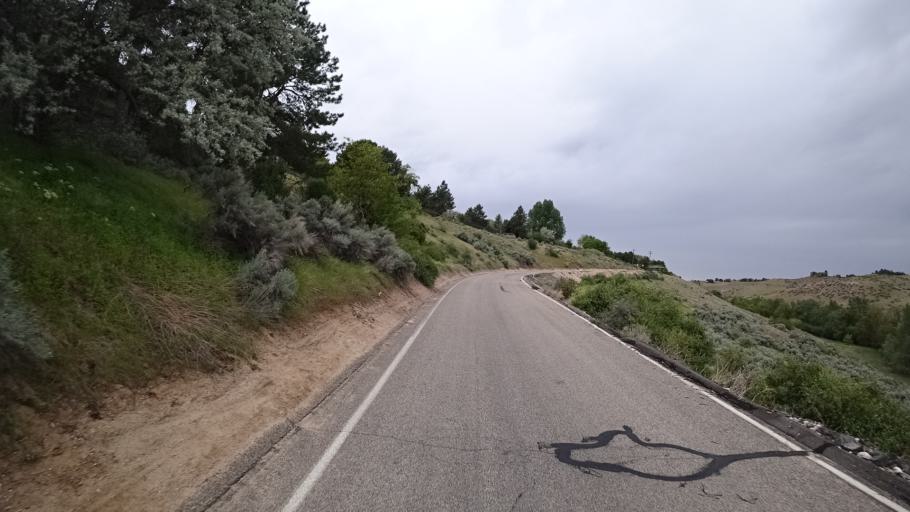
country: US
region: Idaho
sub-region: Ada County
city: Boise
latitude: 43.6164
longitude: -116.1642
